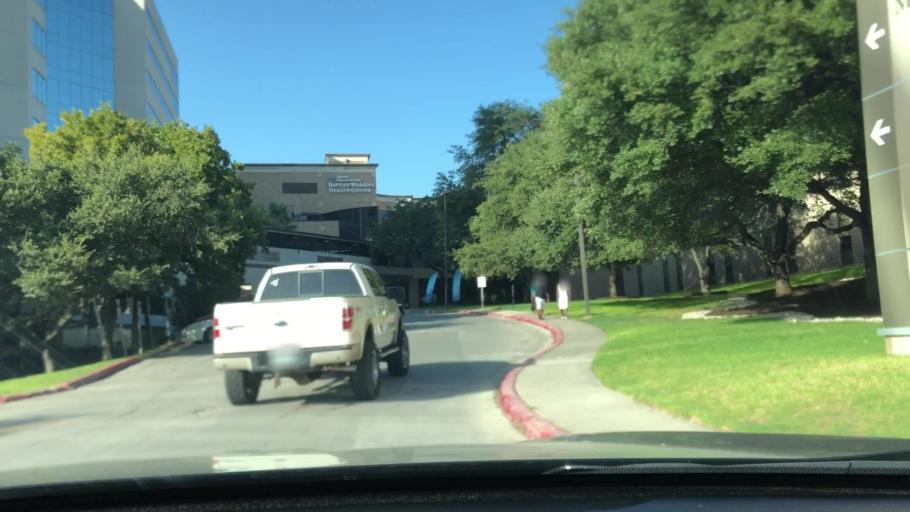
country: US
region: Texas
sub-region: Bexar County
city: Balcones Heights
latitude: 29.5119
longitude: -98.5758
